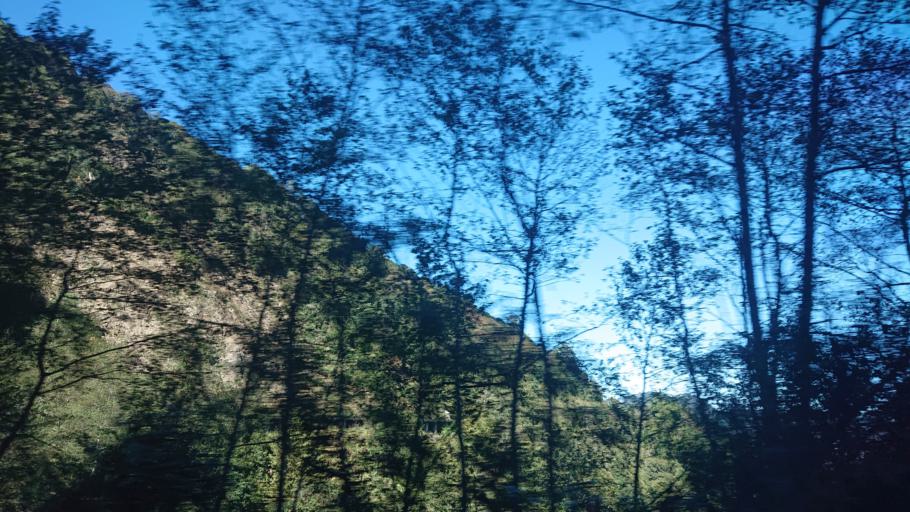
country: TW
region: Taiwan
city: Lugu
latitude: 23.4737
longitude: 120.8395
